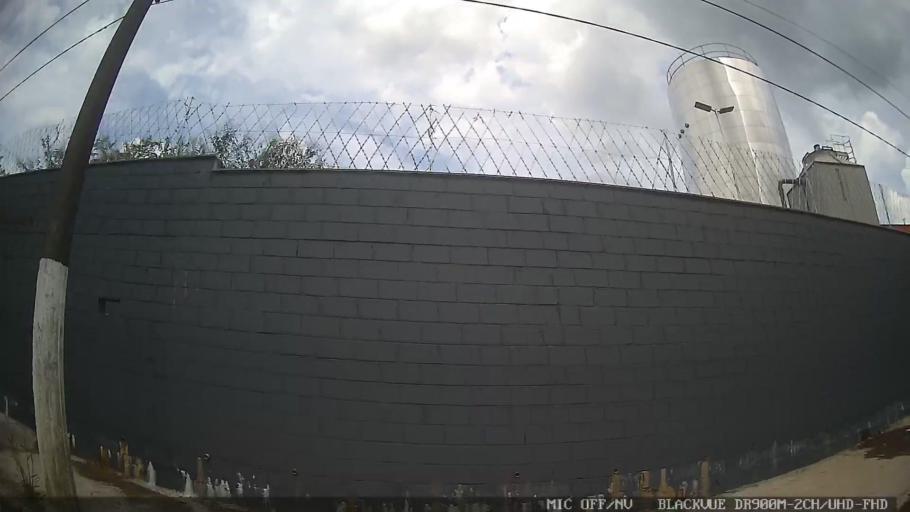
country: BR
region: Sao Paulo
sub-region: Ribeirao Pires
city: Ribeirao Pires
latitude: -23.7046
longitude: -46.3990
